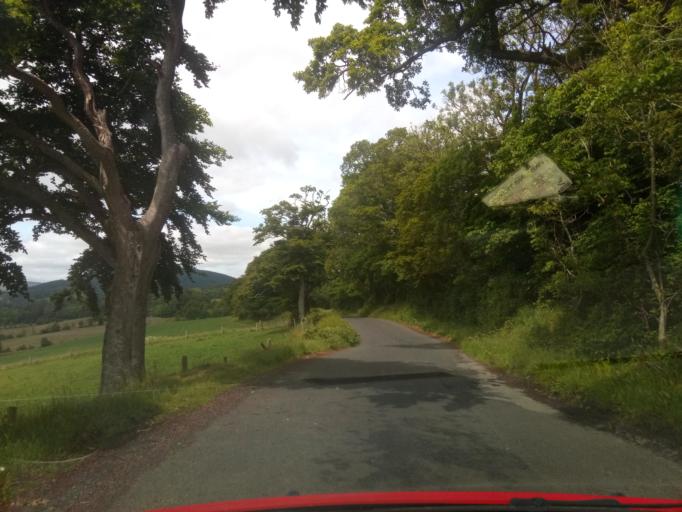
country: GB
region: Scotland
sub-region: The Scottish Borders
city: Selkirk
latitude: 55.5832
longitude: -2.8344
